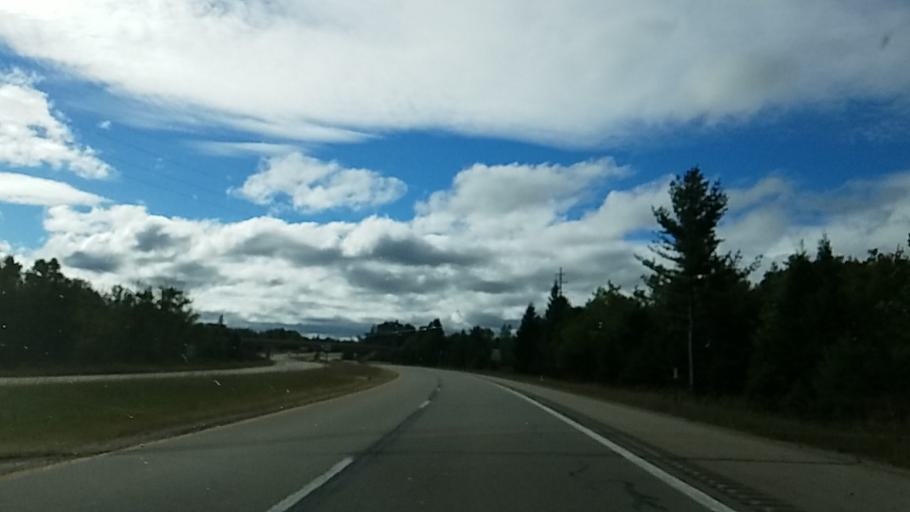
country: US
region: Michigan
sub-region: Mackinac County
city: Saint Ignace
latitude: 45.7648
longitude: -84.7344
